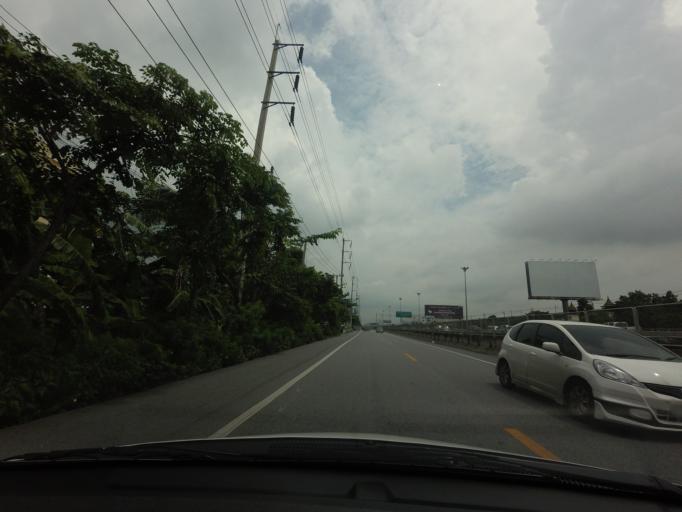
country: TH
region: Bangkok
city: Suan Luang
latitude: 13.7358
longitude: 100.6766
